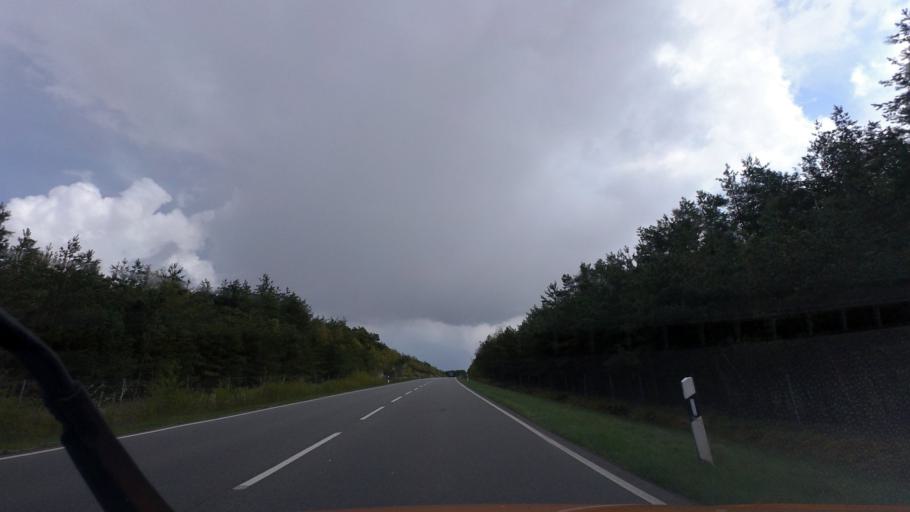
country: DE
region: Lower Saxony
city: Embsen
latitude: 53.1935
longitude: 10.3581
